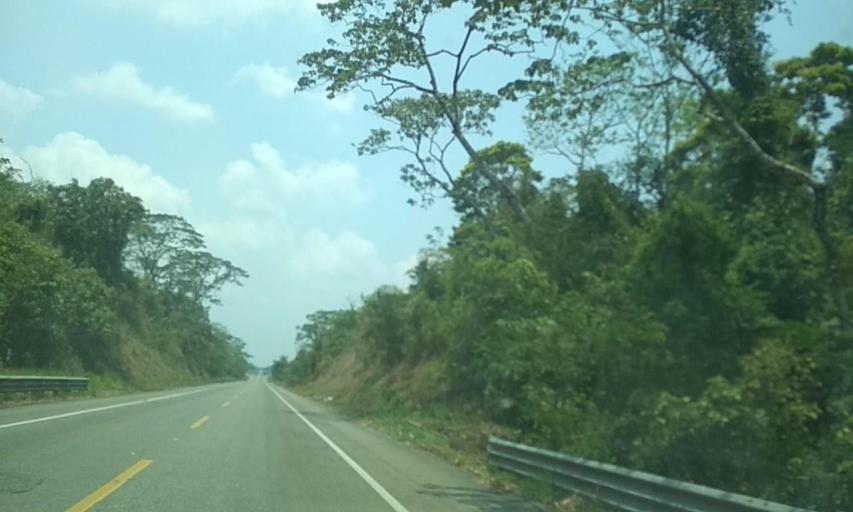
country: MX
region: Tabasco
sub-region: Huimanguillo
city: Francisco Rueda
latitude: 17.6651
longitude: -93.8609
